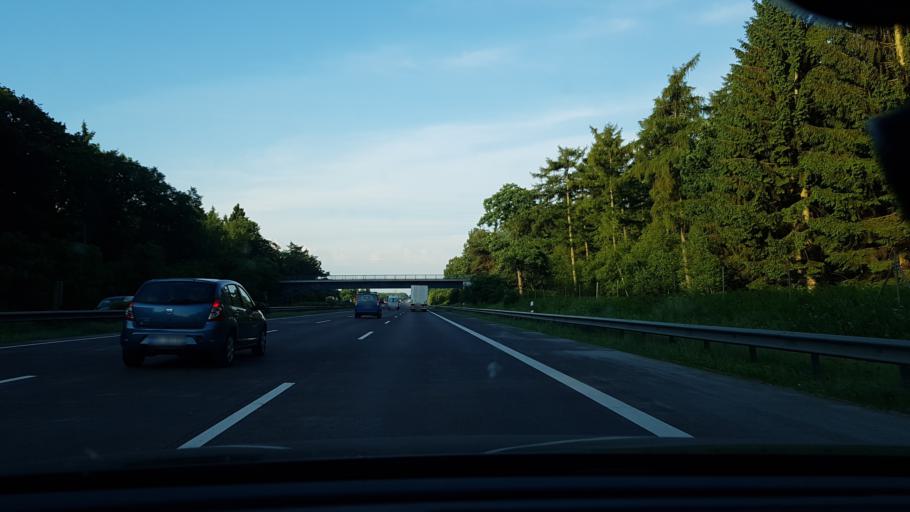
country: DE
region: Schleswig-Holstein
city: Hammoor
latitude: 53.6868
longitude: 10.3175
